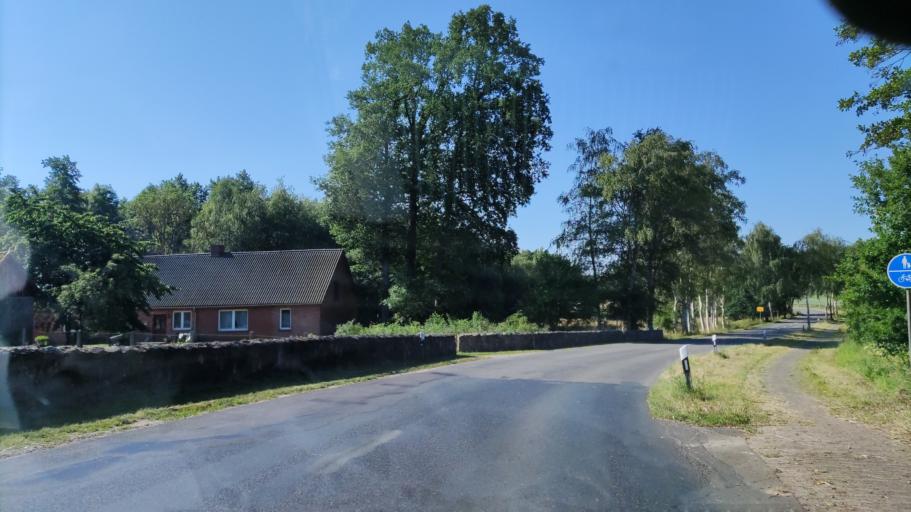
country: DE
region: Lower Saxony
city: Eimke
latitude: 52.9731
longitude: 10.3141
